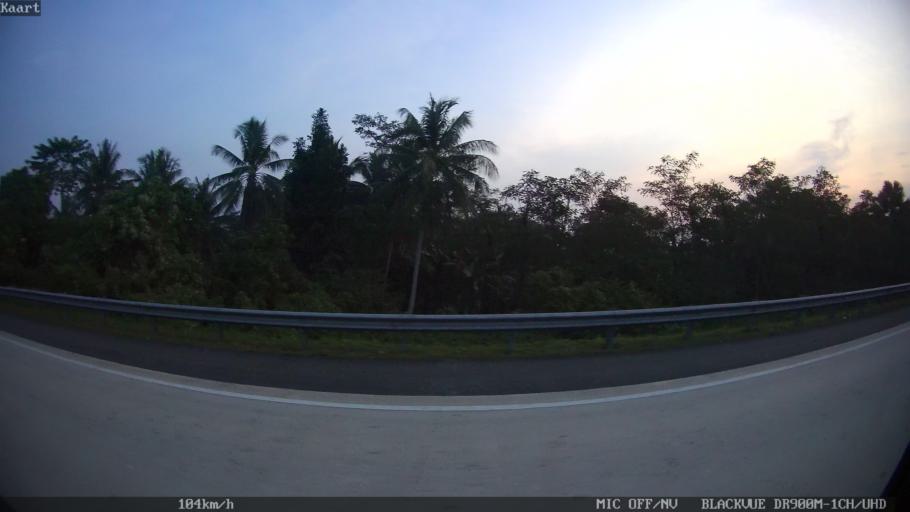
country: ID
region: Lampung
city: Pasuruan
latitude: -5.7072
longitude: 105.6420
